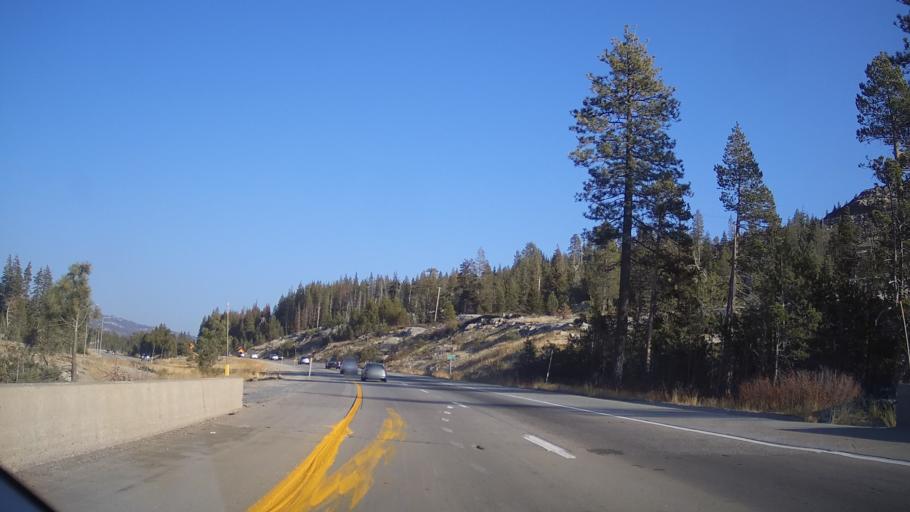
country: US
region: California
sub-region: Nevada County
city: Truckee
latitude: 39.3135
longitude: -120.4699
